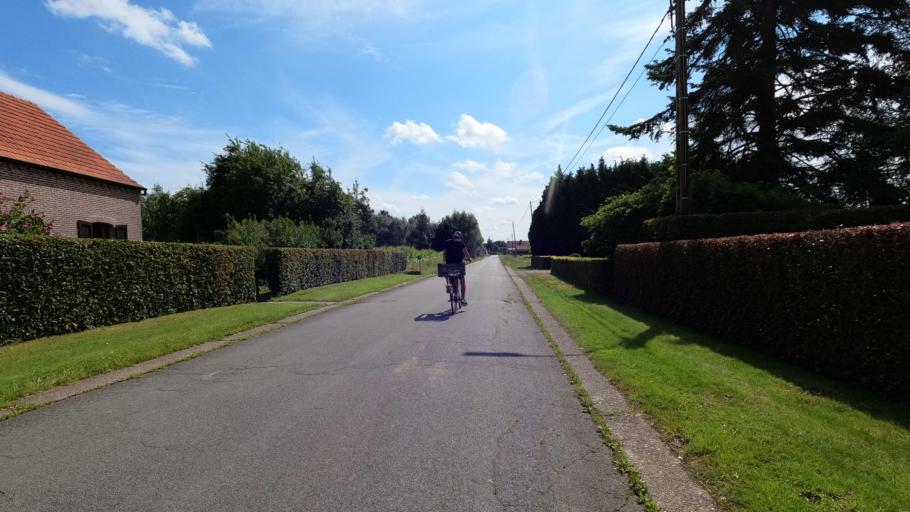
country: BE
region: Flanders
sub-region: Provincie Antwerpen
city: Heist-op-den-Berg
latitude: 51.0584
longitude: 4.7583
